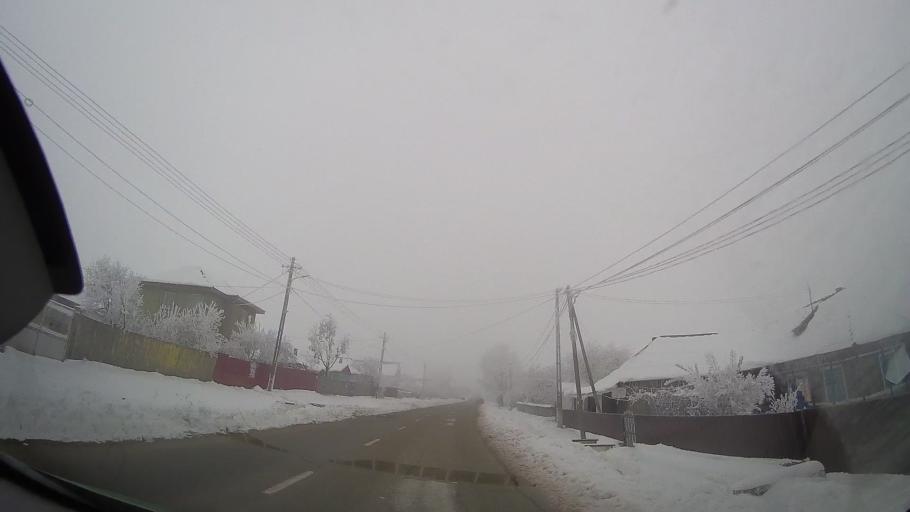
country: RO
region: Neamt
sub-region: Comuna Valea Ursului
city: Valea Ursului
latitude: 46.7980
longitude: 27.0779
